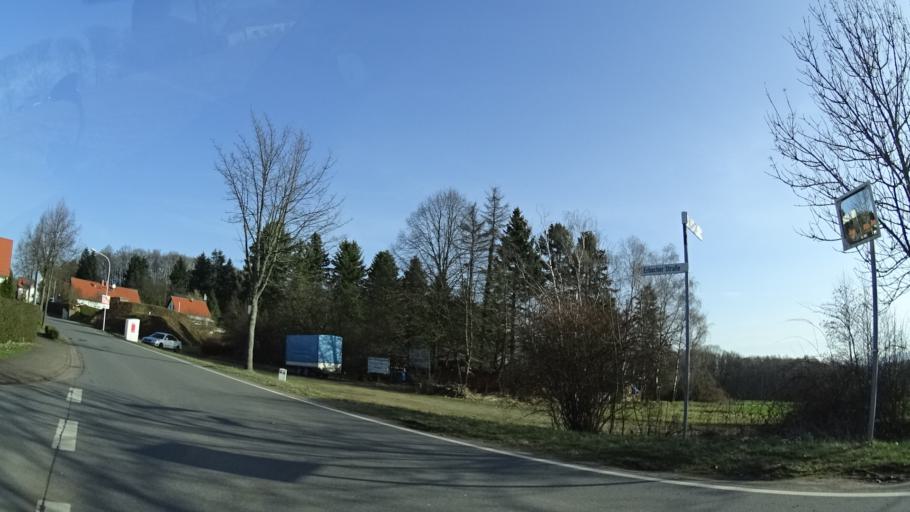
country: DE
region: Hesse
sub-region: Regierungsbezirk Darmstadt
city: Brensbach
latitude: 49.7374
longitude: 8.9207
